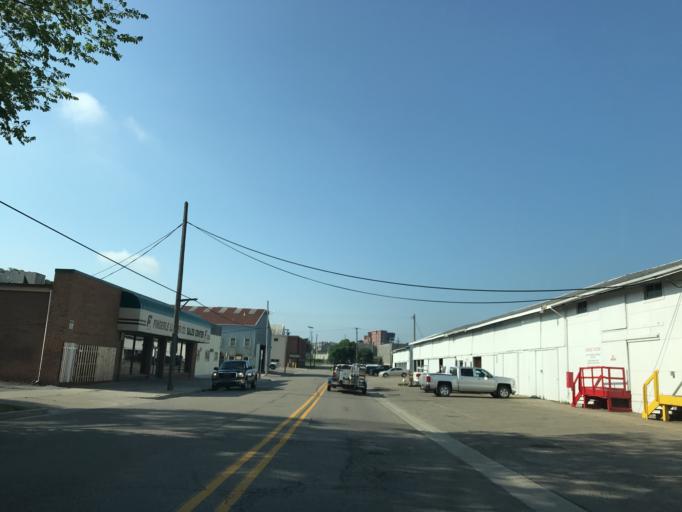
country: US
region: Michigan
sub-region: Washtenaw County
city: Ann Arbor
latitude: 42.2738
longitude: -83.7465
